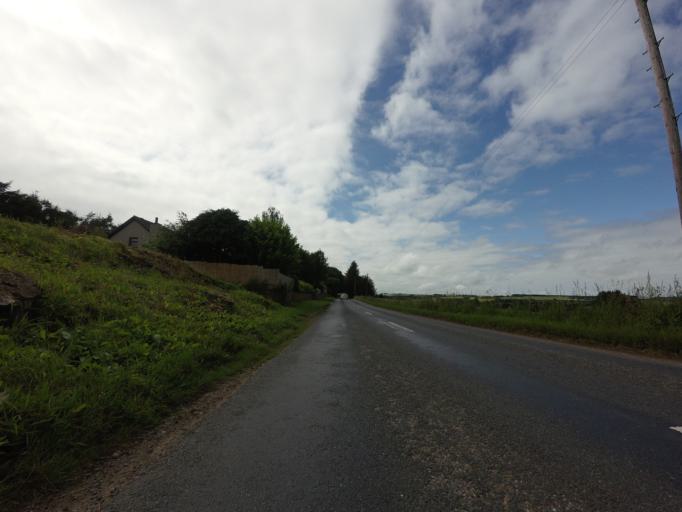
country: GB
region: Scotland
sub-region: Aberdeenshire
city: Turriff
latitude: 57.5424
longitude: -2.3125
